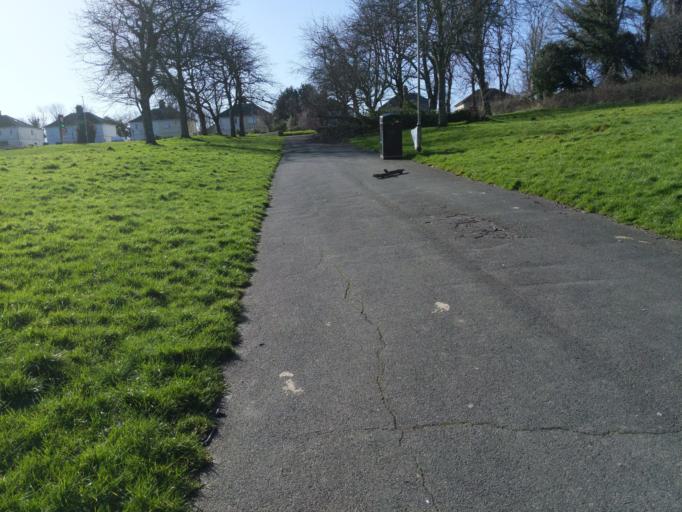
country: GB
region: England
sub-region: Plymouth
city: Plymouth
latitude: 50.4137
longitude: -4.1524
